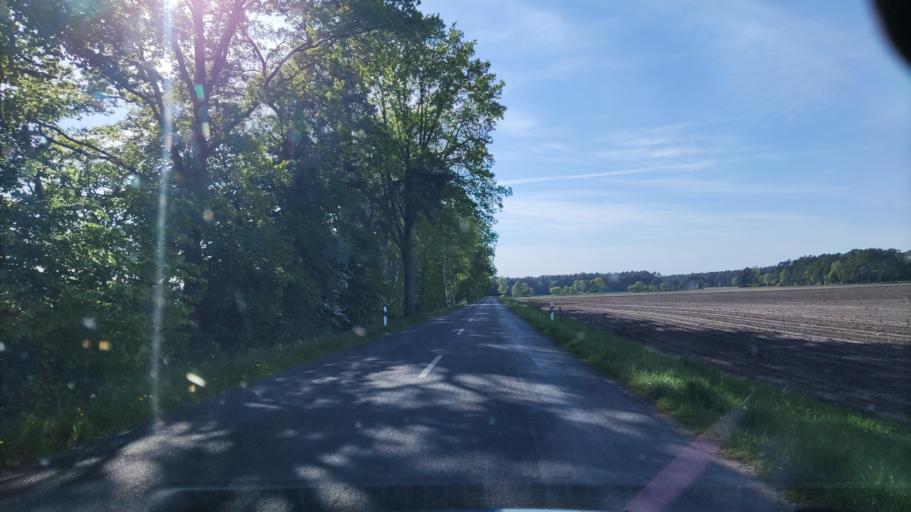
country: DE
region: Lower Saxony
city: Schneverdingen
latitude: 53.1788
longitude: 9.7807
